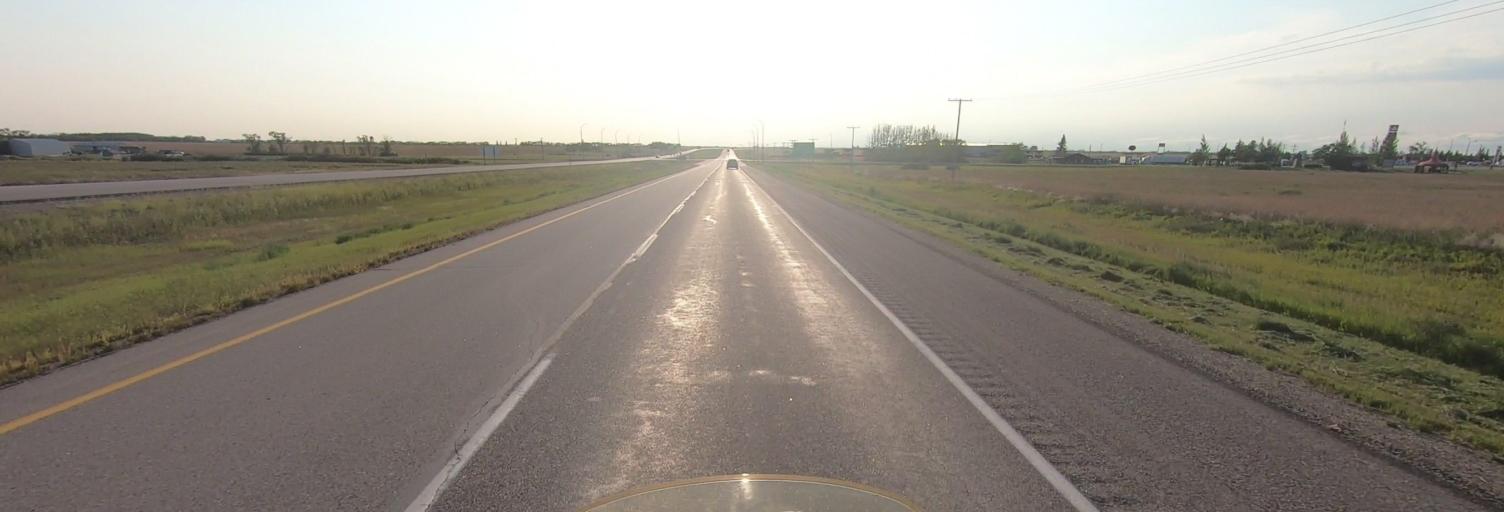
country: CA
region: Saskatchewan
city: Indian Head
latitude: 50.5253
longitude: -103.6733
